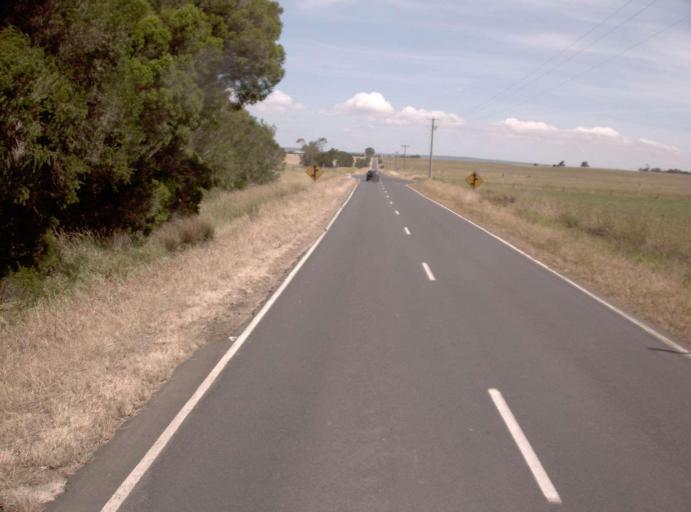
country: AU
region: Victoria
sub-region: Wellington
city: Heyfield
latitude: -38.1004
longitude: 146.8644
